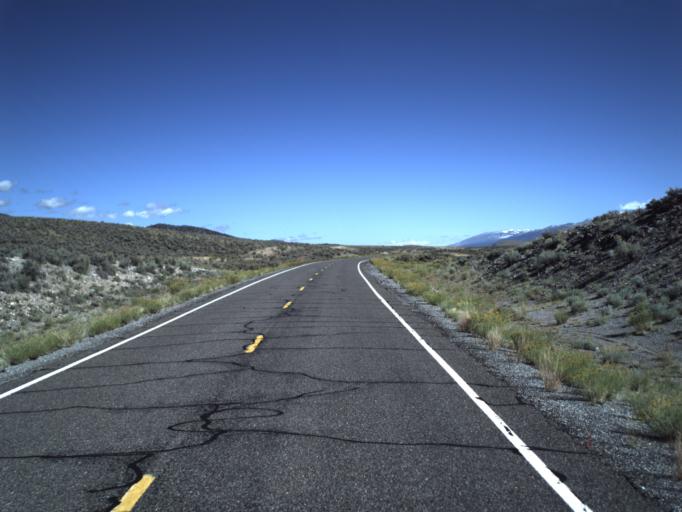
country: US
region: Utah
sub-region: Piute County
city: Junction
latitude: 38.3141
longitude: -111.9668
